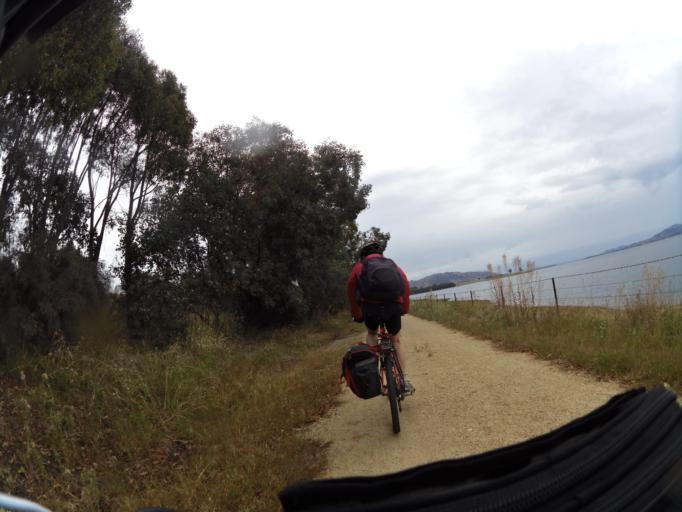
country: AU
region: New South Wales
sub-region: Albury Municipality
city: East Albury
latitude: -36.2215
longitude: 147.0712
